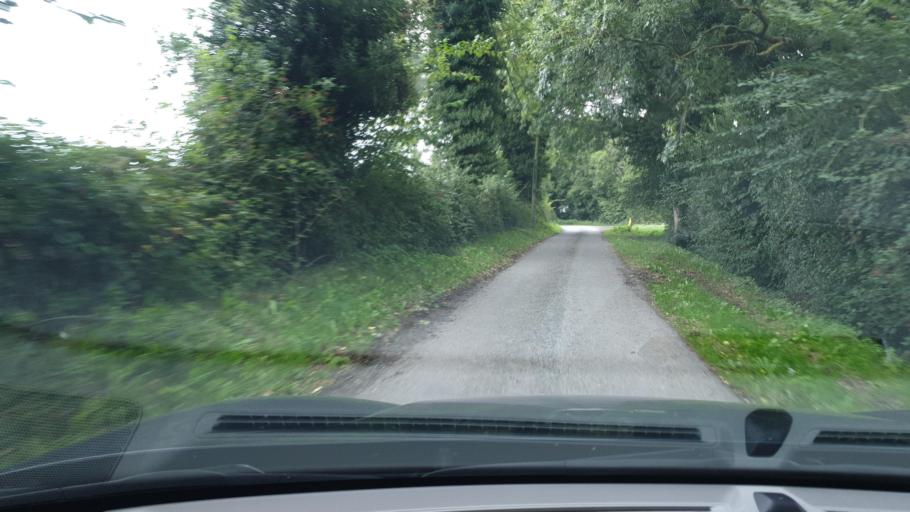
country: IE
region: Leinster
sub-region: Kildare
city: Maynooth
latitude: 53.3368
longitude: -6.6389
